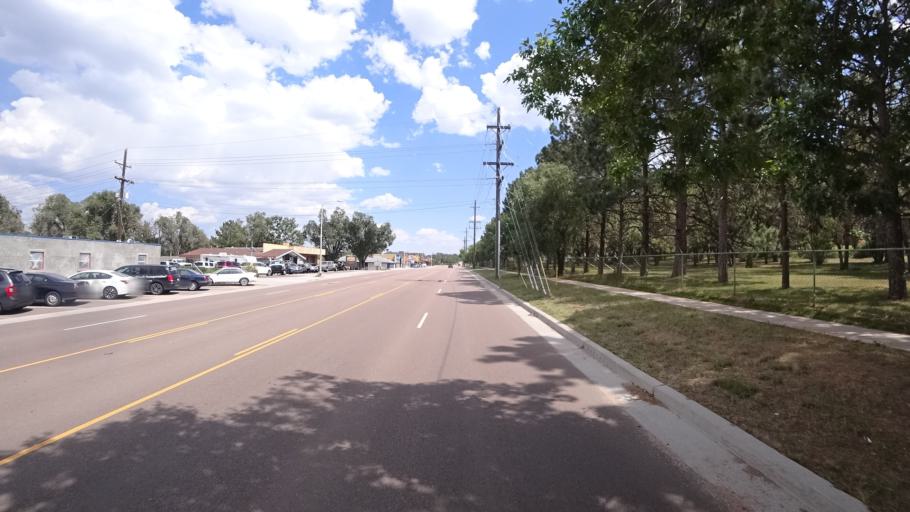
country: US
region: Colorado
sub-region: El Paso County
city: Colorado Springs
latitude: 38.8329
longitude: -104.7929
